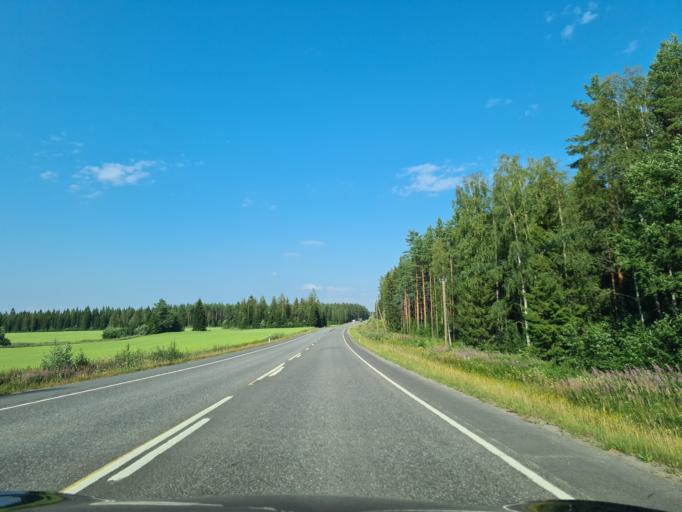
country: FI
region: Satakunta
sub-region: Pohjois-Satakunta
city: Kankaanpaeae
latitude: 61.8259
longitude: 22.3859
